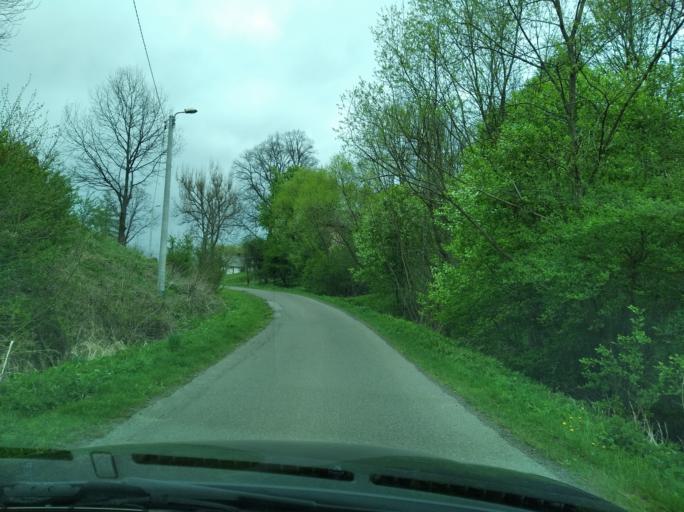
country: PL
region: Subcarpathian Voivodeship
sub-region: Powiat brzozowski
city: Dydnia
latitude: 49.6688
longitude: 22.2506
